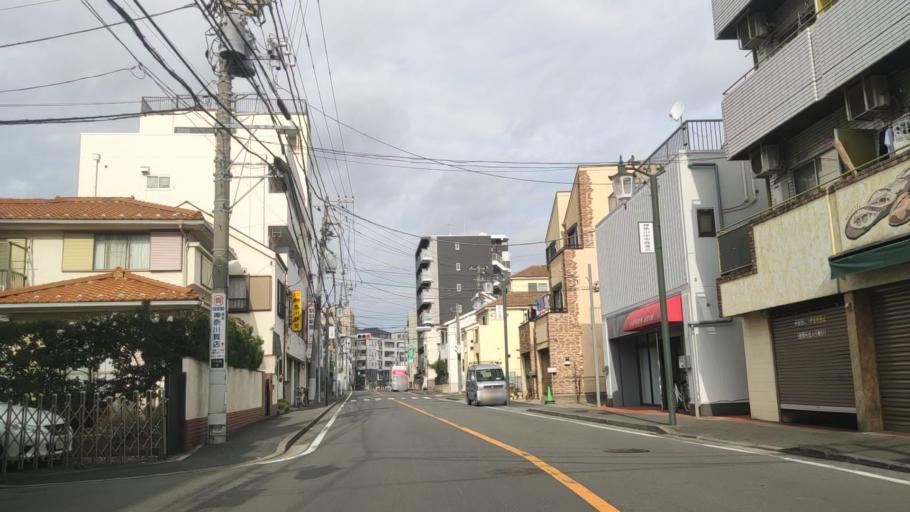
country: JP
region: Kanagawa
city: Yokohama
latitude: 35.4801
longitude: 139.6278
